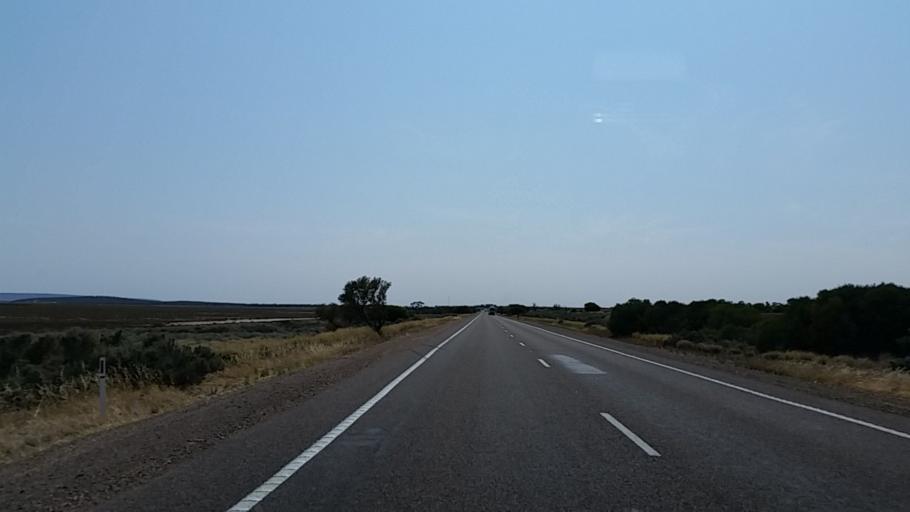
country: AU
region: South Australia
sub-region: Port Augusta
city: Port Augusta
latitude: -32.7600
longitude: 137.9511
